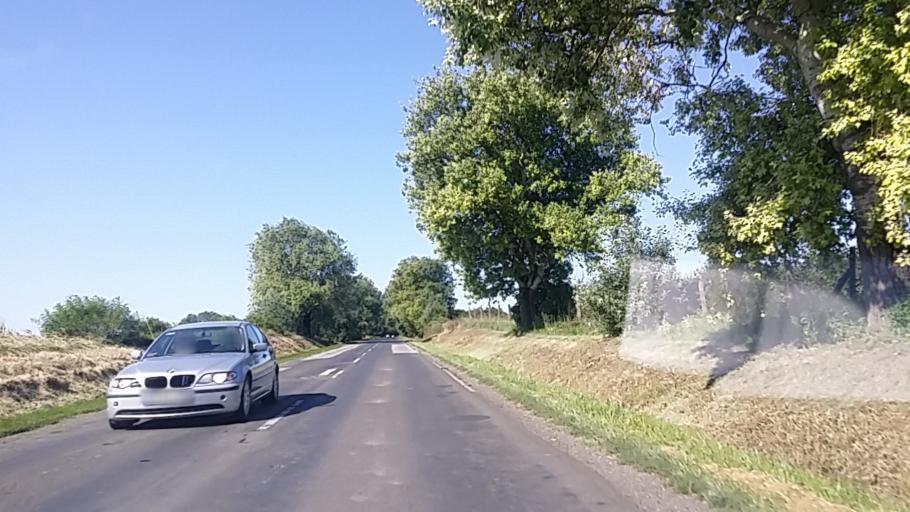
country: HU
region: Fejer
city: Mezofalva
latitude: 46.9476
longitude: 18.8371
